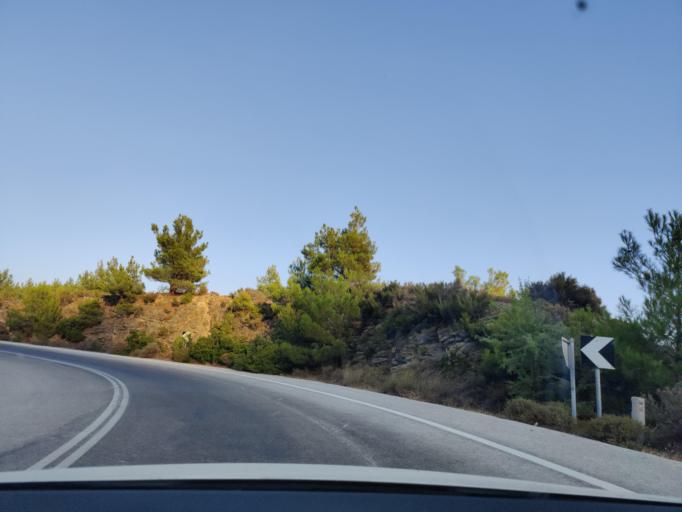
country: GR
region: East Macedonia and Thrace
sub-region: Nomos Kavalas
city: Potamia
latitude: 40.6245
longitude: 24.7640
